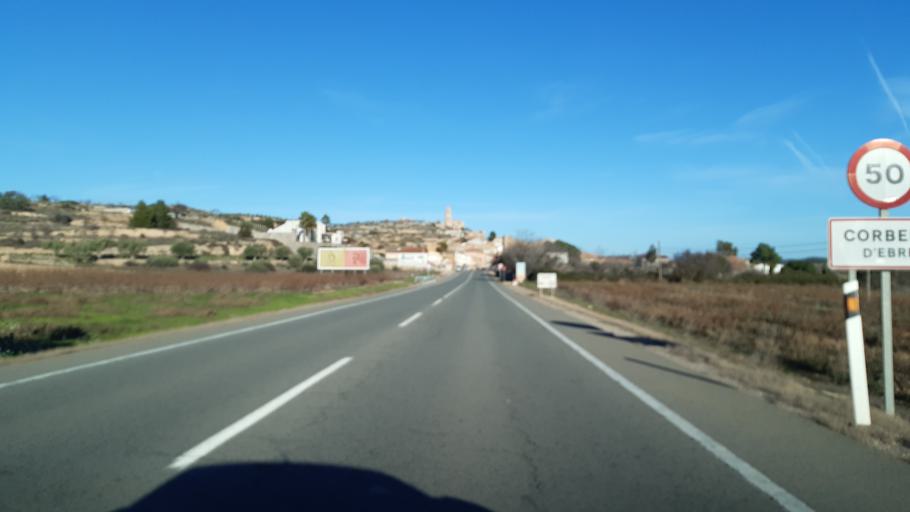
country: ES
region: Catalonia
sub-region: Provincia de Tarragona
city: Gandesa
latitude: 41.0730
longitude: 0.4671
